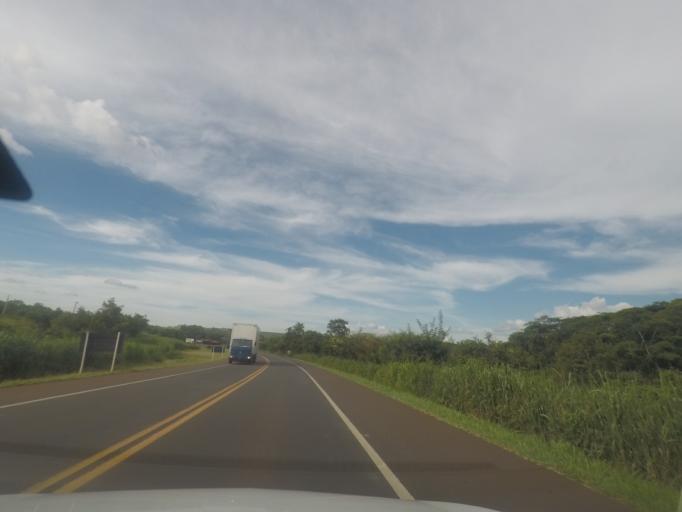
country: BR
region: Minas Gerais
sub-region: Monte Alegre De Minas
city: Monte Alegre de Minas
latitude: -19.0459
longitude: -49.0104
